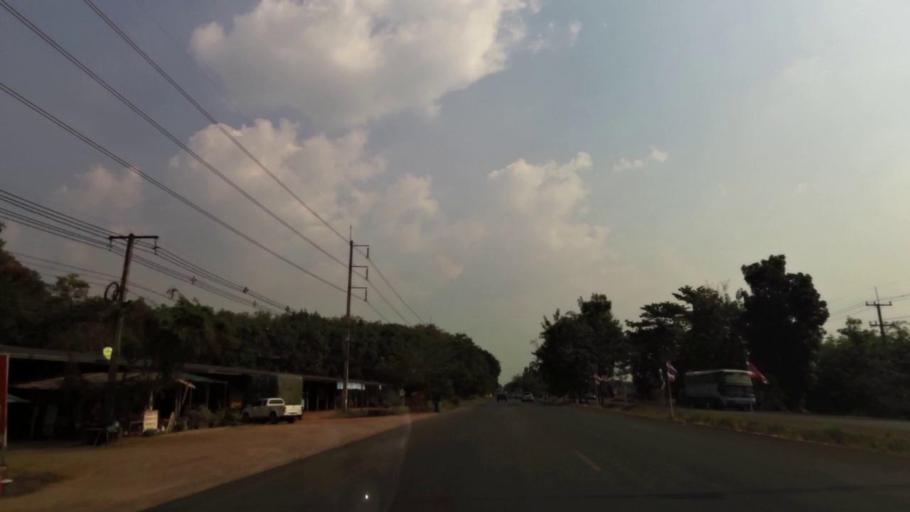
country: TH
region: Rayong
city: Wang Chan
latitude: 12.8943
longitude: 101.5468
